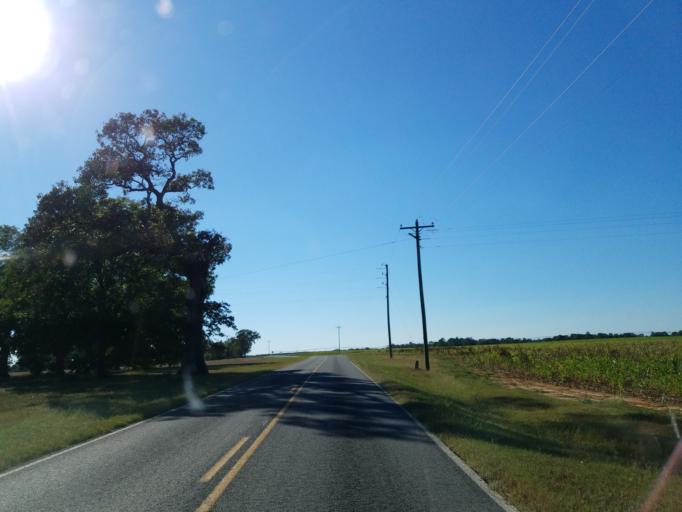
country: US
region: Georgia
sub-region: Dooly County
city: Unadilla
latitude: 32.2447
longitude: -83.8208
